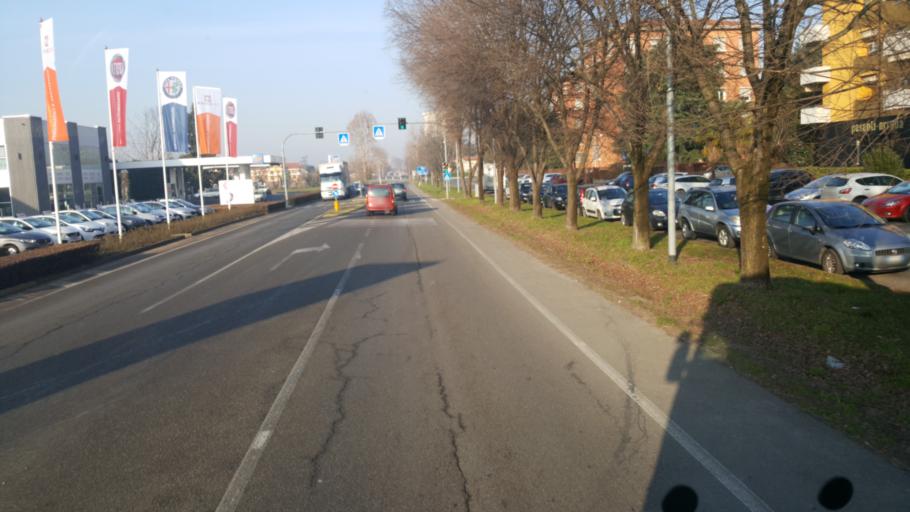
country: IT
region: Lombardy
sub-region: Citta metropolitana di Milano
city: Inzago
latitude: 45.5356
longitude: 9.4863
